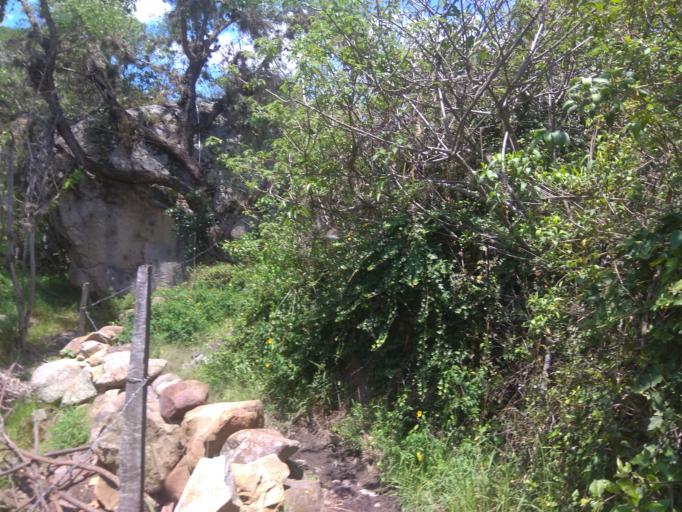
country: CO
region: Boyaca
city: Socha Viejo
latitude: 5.9986
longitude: -72.7146
